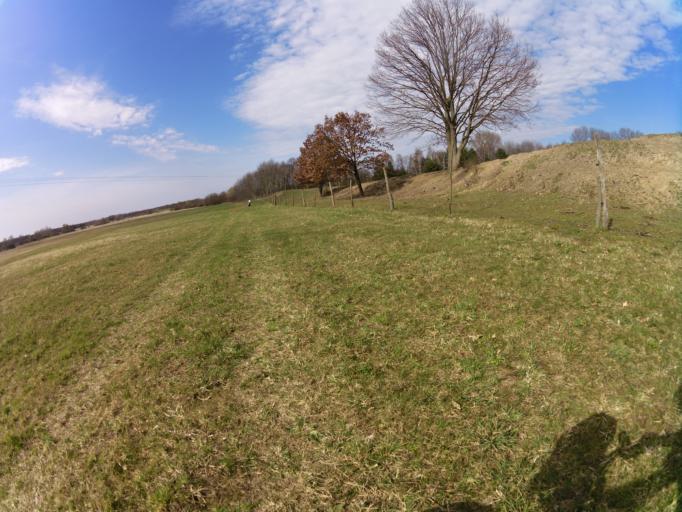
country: PL
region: West Pomeranian Voivodeship
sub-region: Powiat mysliborski
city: Mysliborz
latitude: 52.9706
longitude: 14.8818
